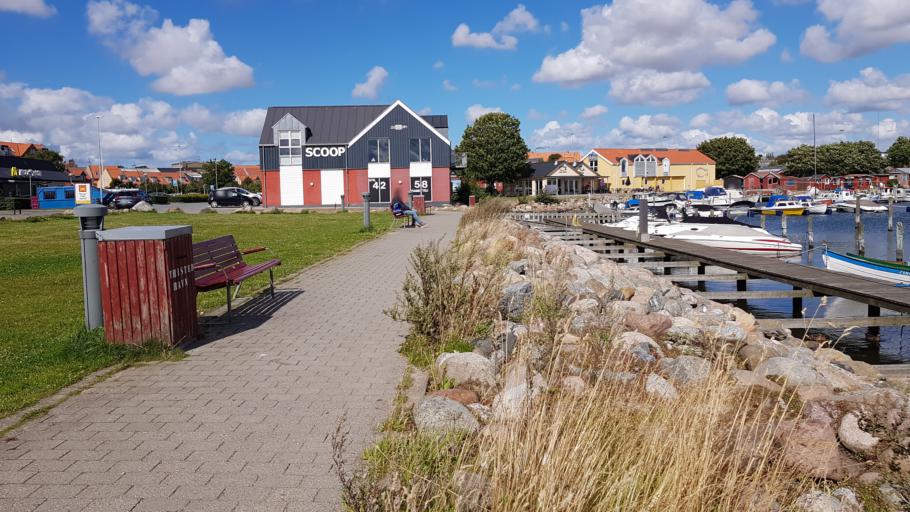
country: DK
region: North Denmark
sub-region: Thisted Kommune
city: Thisted
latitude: 56.9523
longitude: 8.6931
